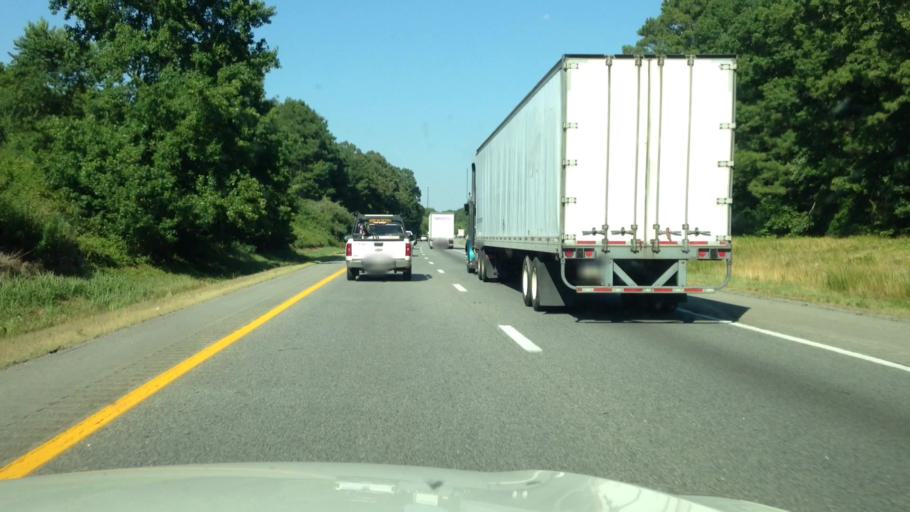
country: US
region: Virginia
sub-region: City of Emporia
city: Emporia
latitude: 36.7620
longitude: -77.4941
